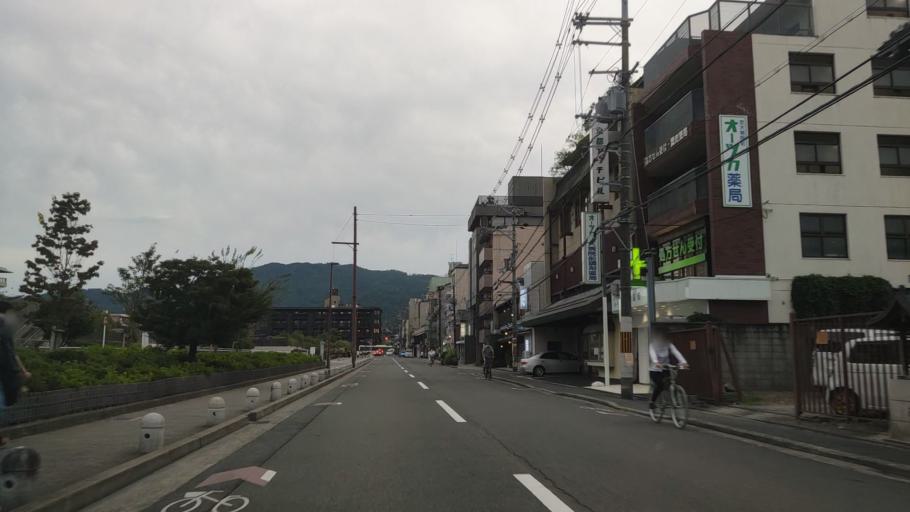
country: JP
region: Kyoto
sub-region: Kyoto-shi
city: Kamigyo-ku
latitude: 35.0185
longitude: 135.7762
